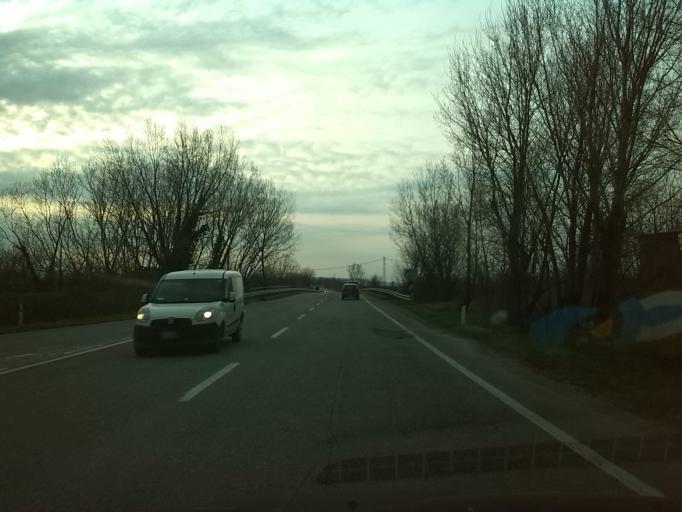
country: IT
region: Friuli Venezia Giulia
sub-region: Provincia di Udine
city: Cividale del Friuli
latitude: 46.0802
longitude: 13.4111
